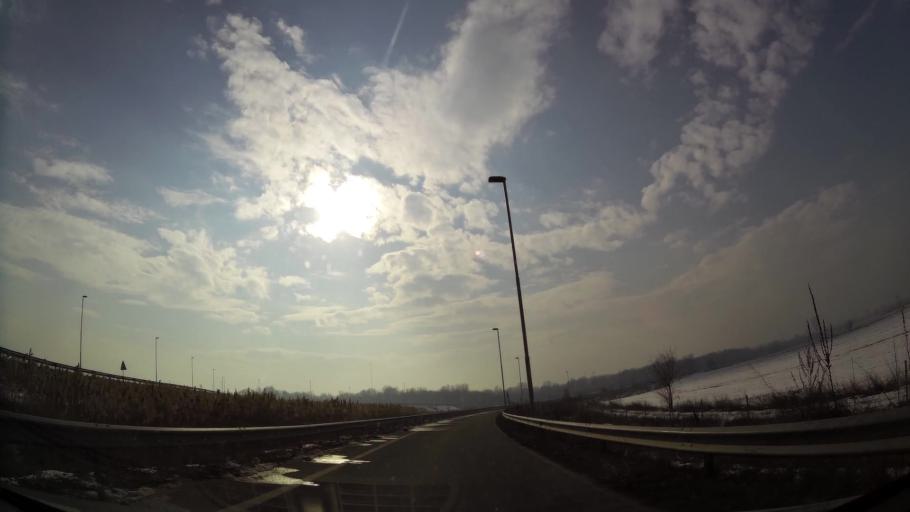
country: MK
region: Ilinden
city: Jurumleri
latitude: 41.9978
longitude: 21.5321
